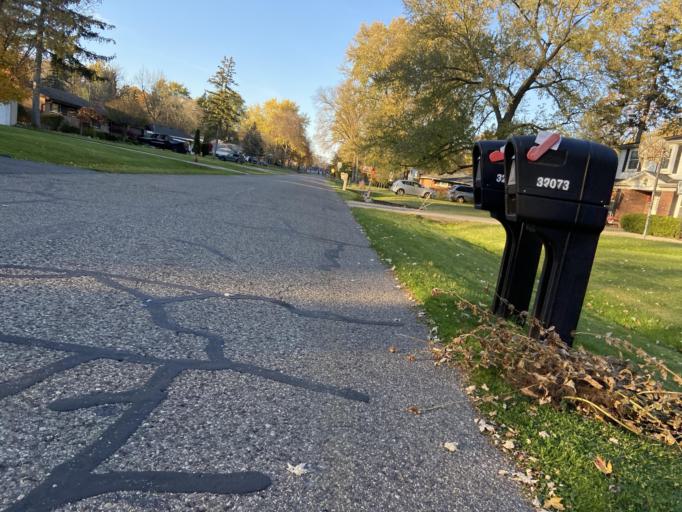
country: US
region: Michigan
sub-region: Oakland County
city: Farmington Hills
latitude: 42.5026
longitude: -83.3643
